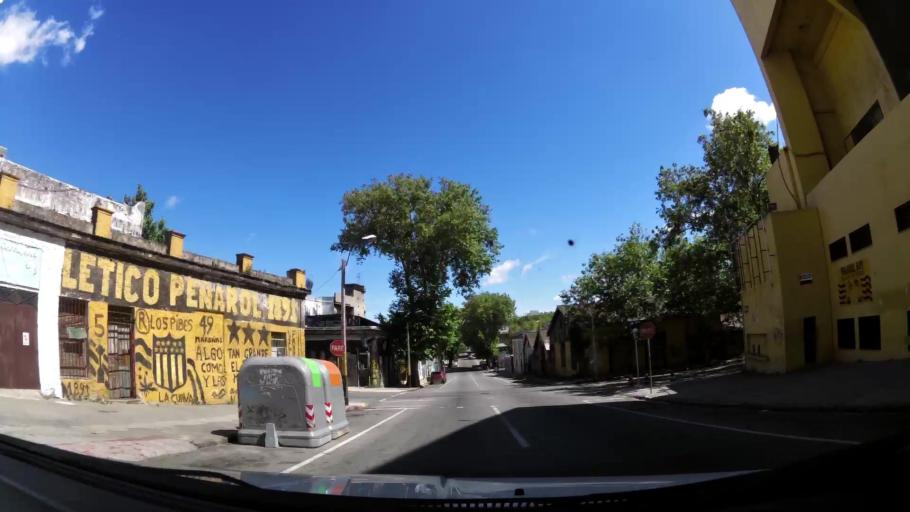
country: UY
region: Montevideo
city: Montevideo
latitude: -34.8989
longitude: -56.1833
